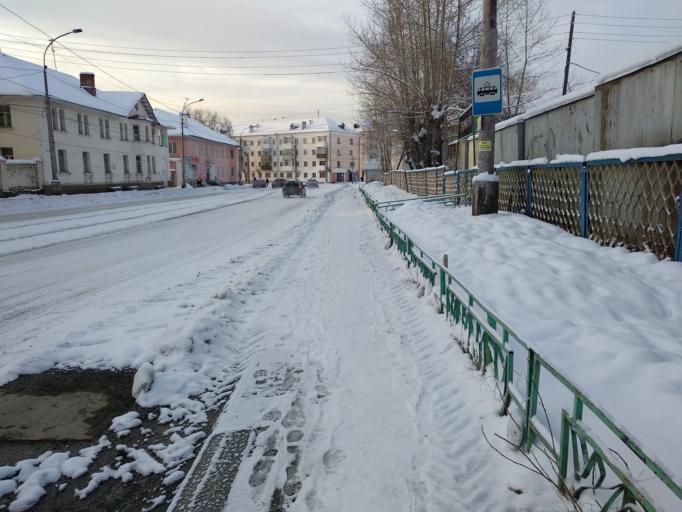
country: RU
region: Sverdlovsk
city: Krasnotur'insk
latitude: 59.7672
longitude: 60.1887
